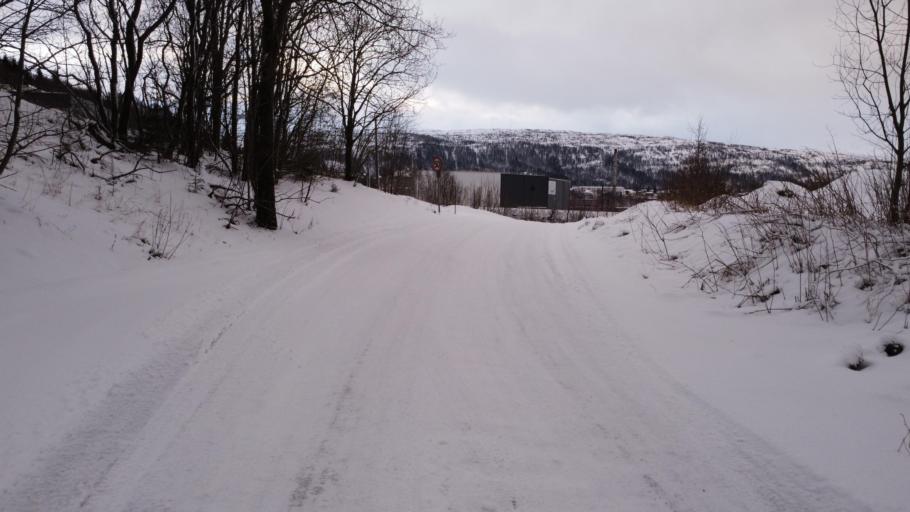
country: NO
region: Nordland
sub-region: Rana
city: Mo i Rana
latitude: 66.3257
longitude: 14.1525
